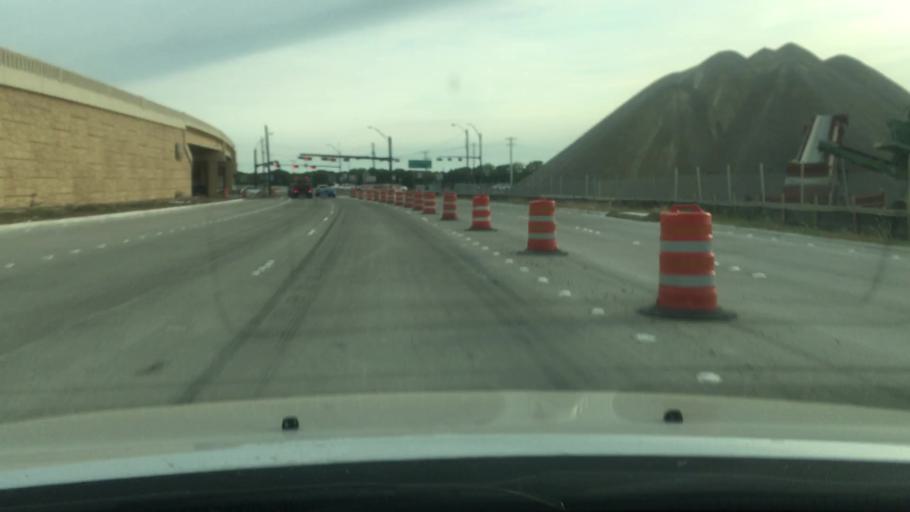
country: US
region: Texas
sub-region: Collin County
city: Prosper
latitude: 33.2200
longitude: -96.8016
